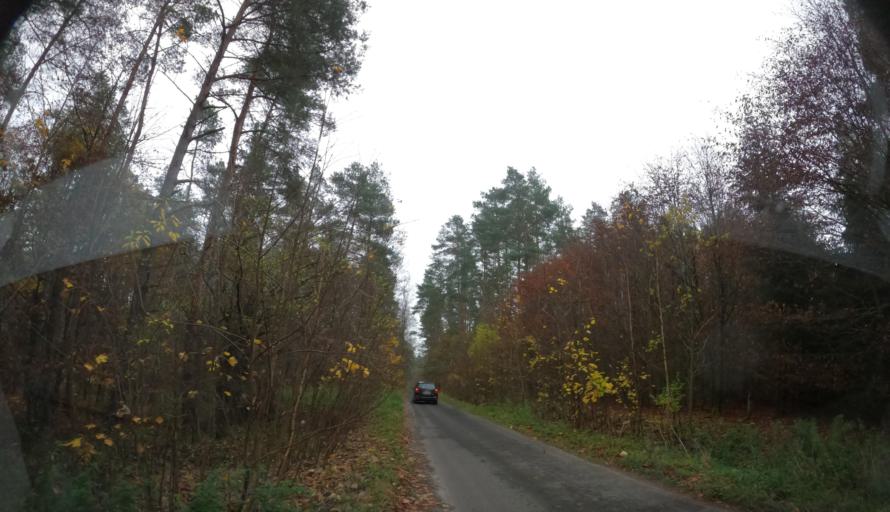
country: PL
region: West Pomeranian Voivodeship
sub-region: Powiat lobeski
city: Radowo Male
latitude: 53.6843
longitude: 15.4601
